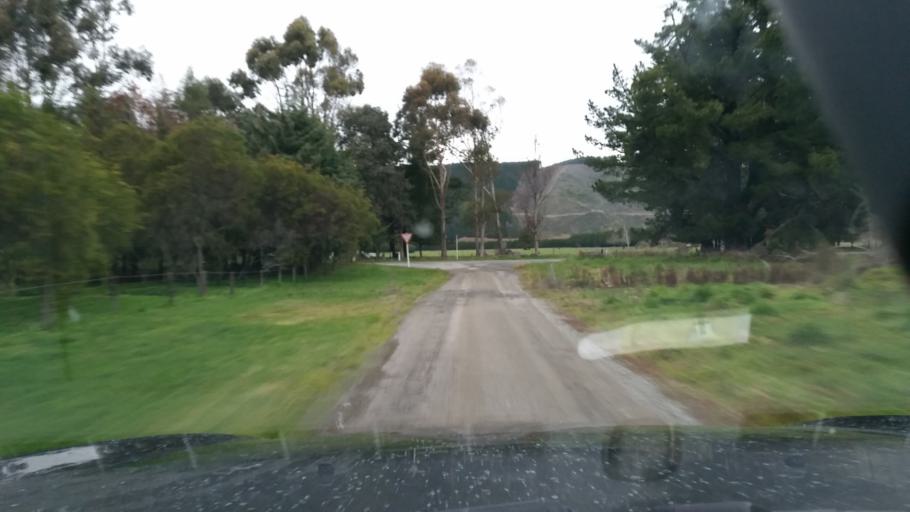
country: NZ
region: Nelson
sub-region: Nelson City
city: Nelson
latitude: -41.5662
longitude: 173.5247
